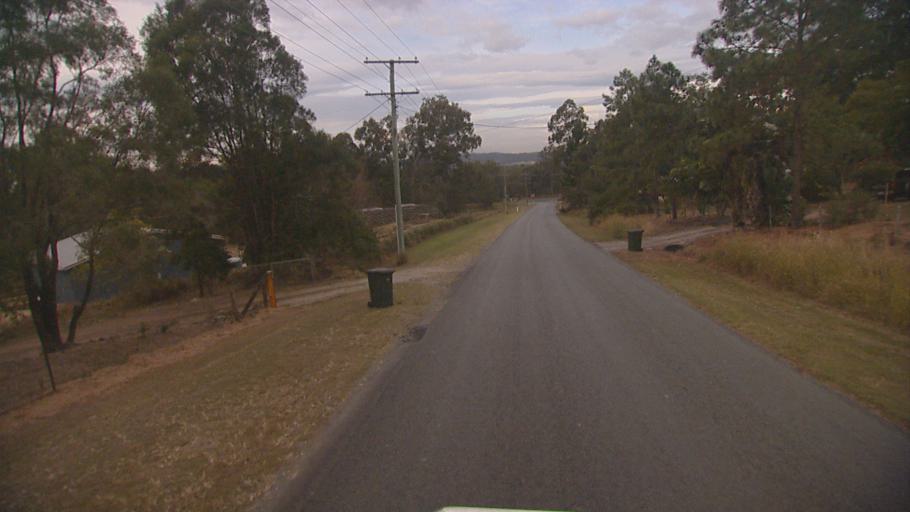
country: AU
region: Queensland
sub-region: Logan
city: Chambers Flat
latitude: -27.8195
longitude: 153.0971
